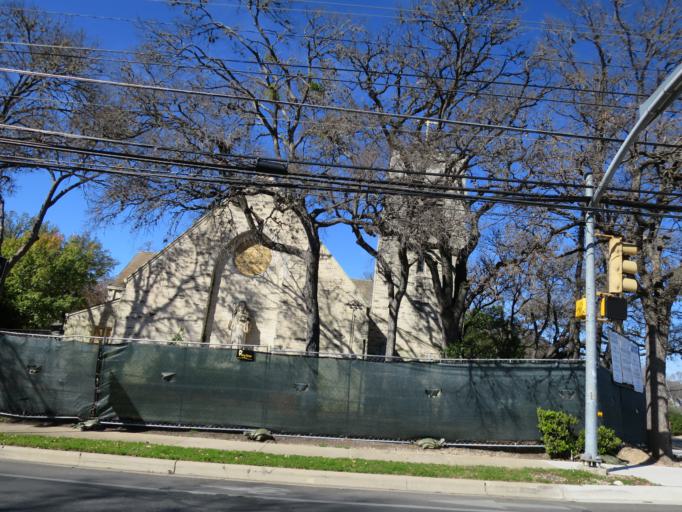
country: US
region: Texas
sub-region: Travis County
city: Rollingwood
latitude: 30.2966
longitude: -97.7683
